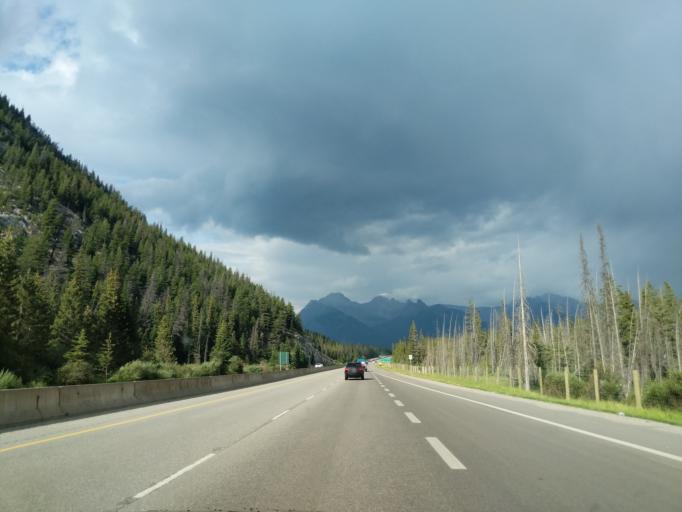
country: CA
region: Alberta
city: Banff
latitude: 51.1900
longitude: -115.5765
